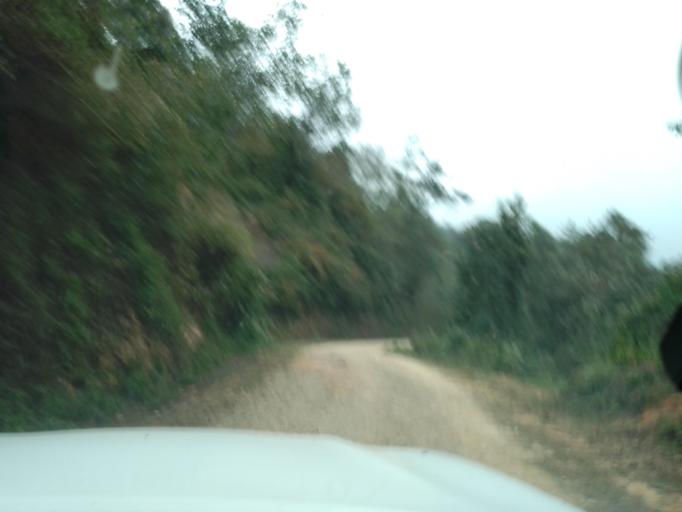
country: MX
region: Chiapas
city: Motozintla de Mendoza
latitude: 15.2165
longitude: -92.2218
